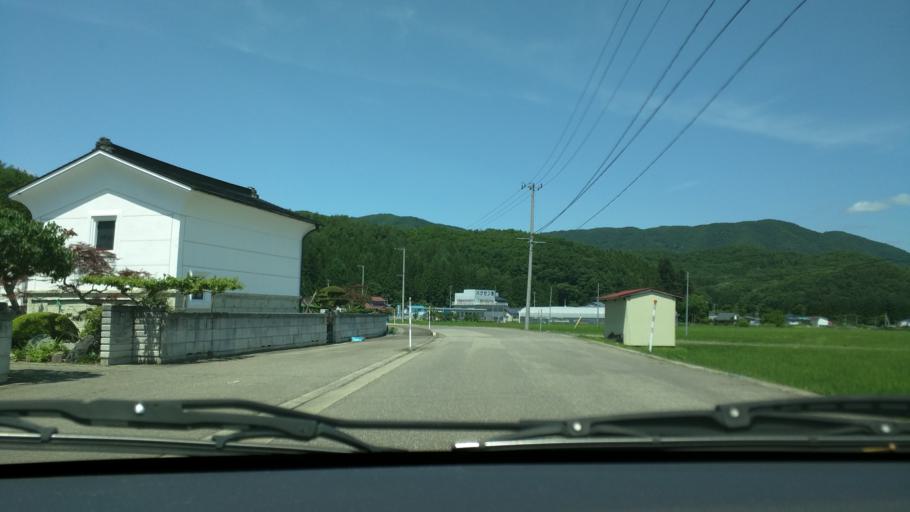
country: JP
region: Tochigi
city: Kuroiso
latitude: 37.2061
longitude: 139.7505
